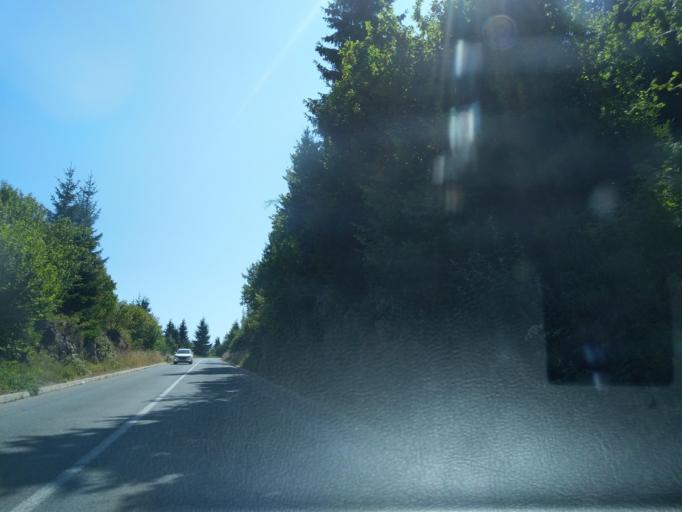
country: RS
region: Central Serbia
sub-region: Zlatiborski Okrug
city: Nova Varos
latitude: 43.4072
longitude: 19.8409
